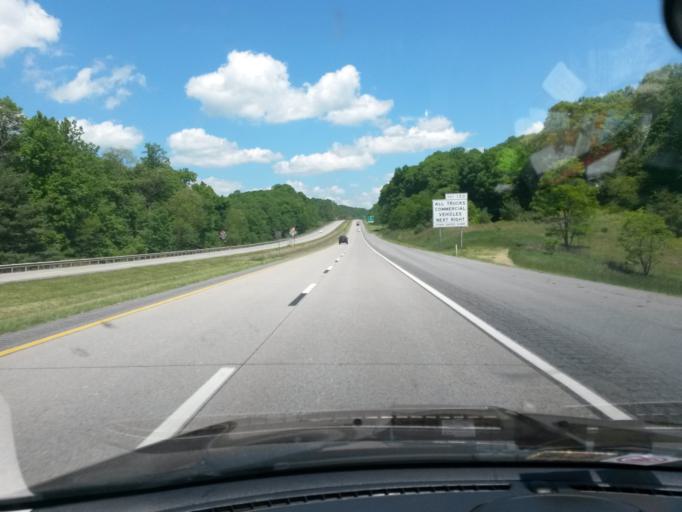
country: US
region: West Virginia
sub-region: Raleigh County
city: Shady Spring
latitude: 37.7667
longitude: -81.0143
